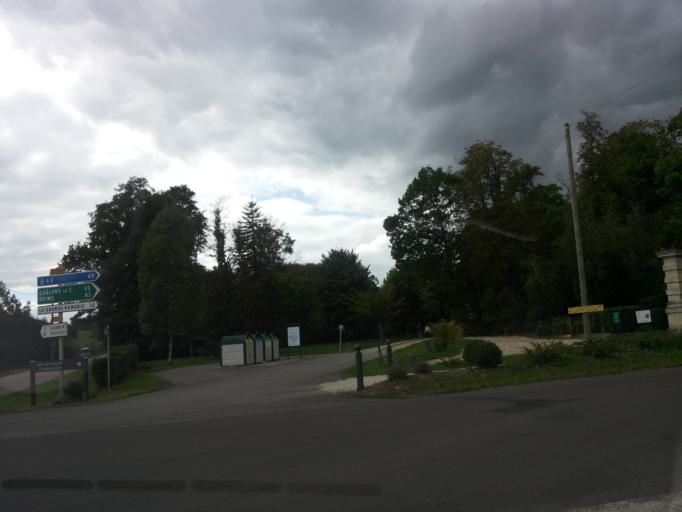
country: FR
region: Lorraine
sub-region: Departement de la Meuse
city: Revigny-sur-Ornain
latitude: 48.8779
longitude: 4.9412
